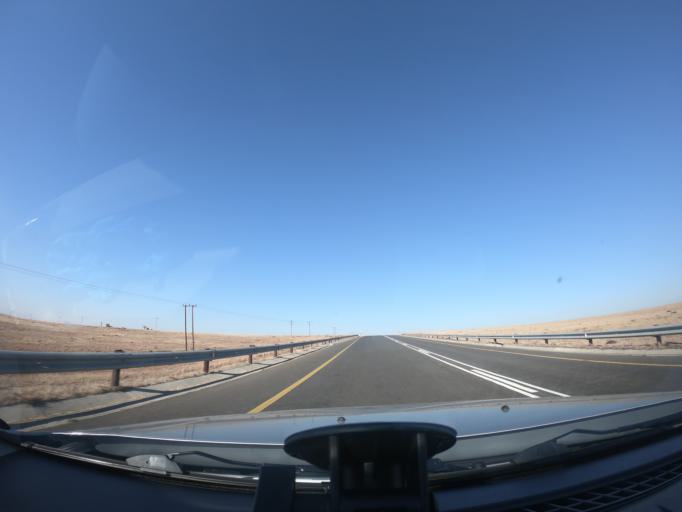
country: ZA
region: Mpumalanga
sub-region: Gert Sibande District Municipality
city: Ermelo
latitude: -26.9140
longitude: 29.8720
